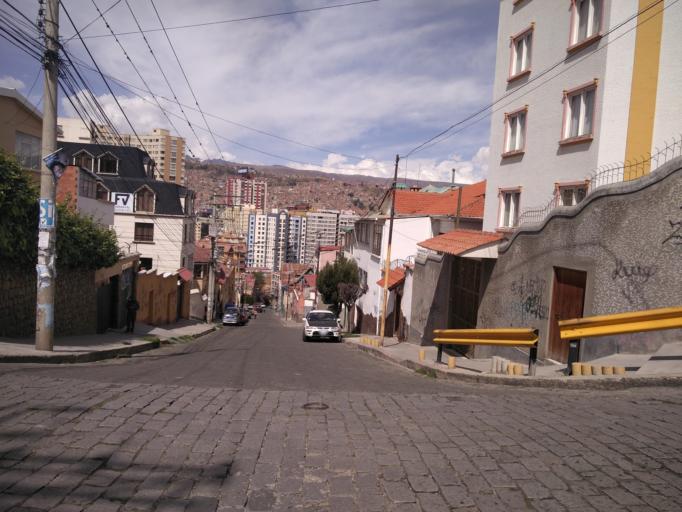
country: BO
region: La Paz
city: La Paz
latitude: -16.5093
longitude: -68.1326
